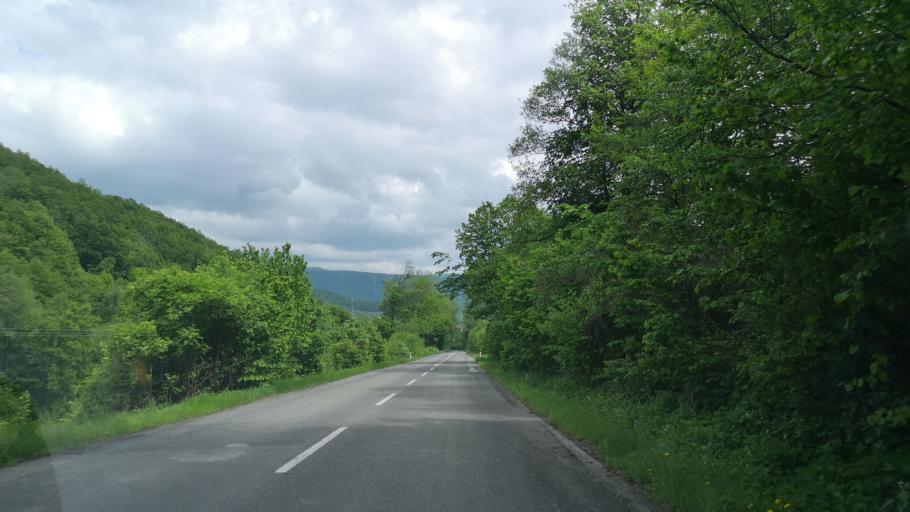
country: SK
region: Kosicky
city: Dobsina
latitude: 48.6383
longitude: 20.3107
